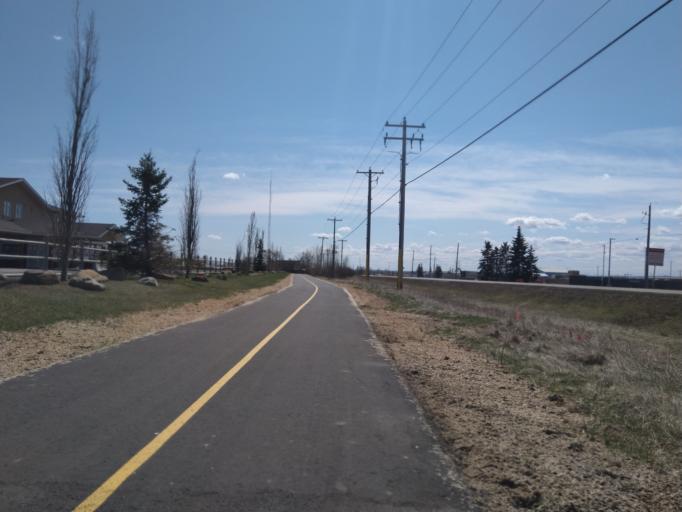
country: CA
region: Alberta
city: Chestermere
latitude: 50.9553
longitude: -113.9116
